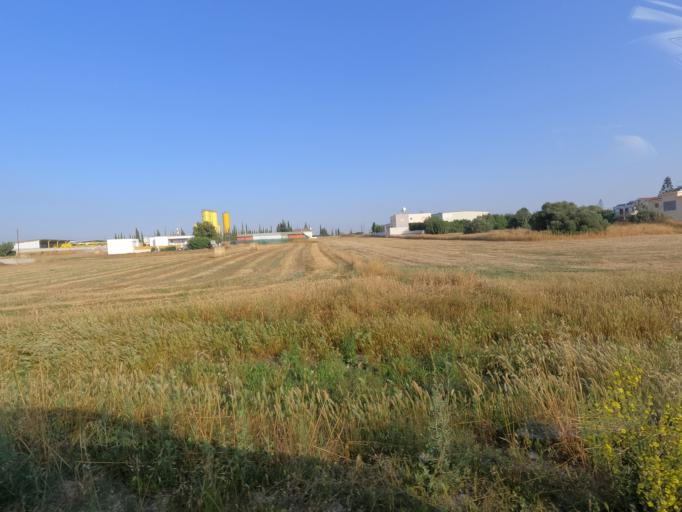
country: CY
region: Ammochostos
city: Paralimni
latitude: 35.0285
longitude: 33.9801
